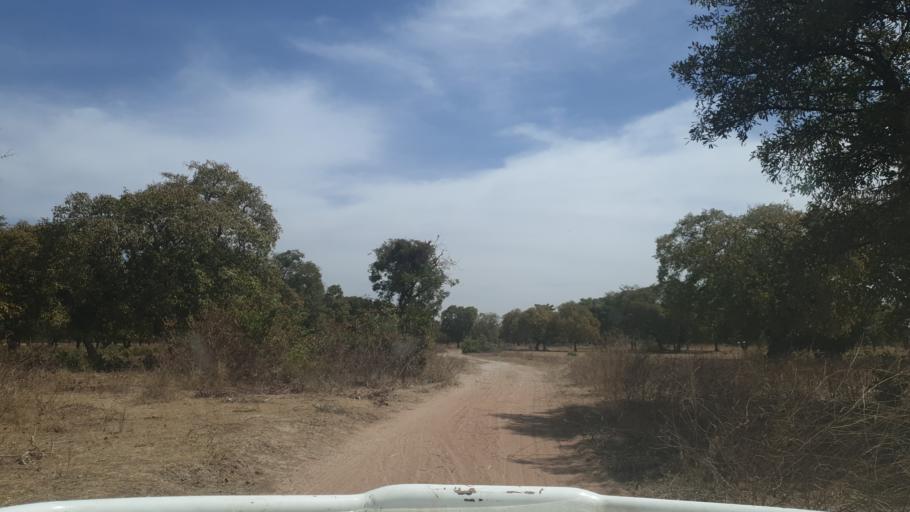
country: ML
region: Sikasso
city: Yorosso
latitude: 12.2922
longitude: -4.6627
